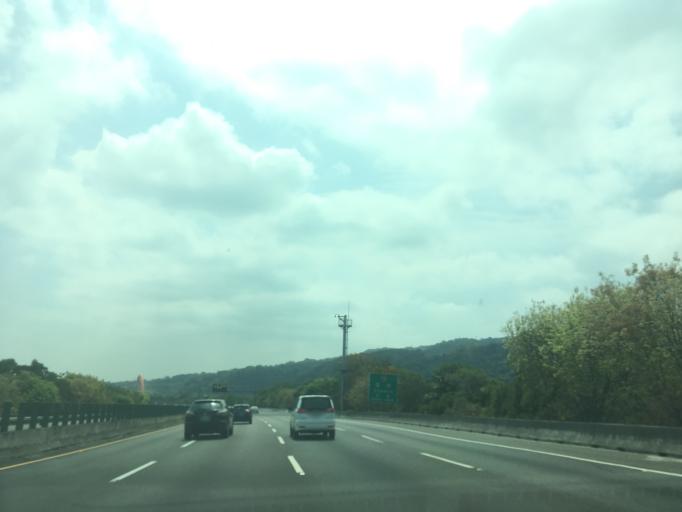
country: TW
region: Taiwan
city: Zhongxing New Village
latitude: 23.9689
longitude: 120.6485
